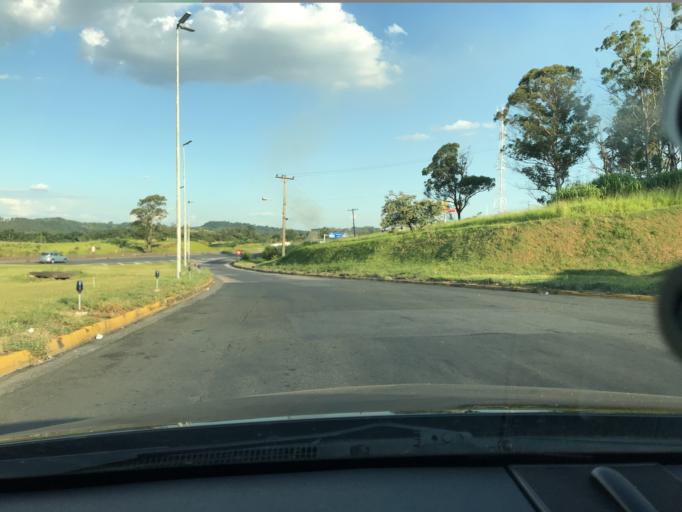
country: BR
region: Sao Paulo
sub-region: Vinhedo
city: Vinhedo
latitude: -23.0410
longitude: -47.0665
